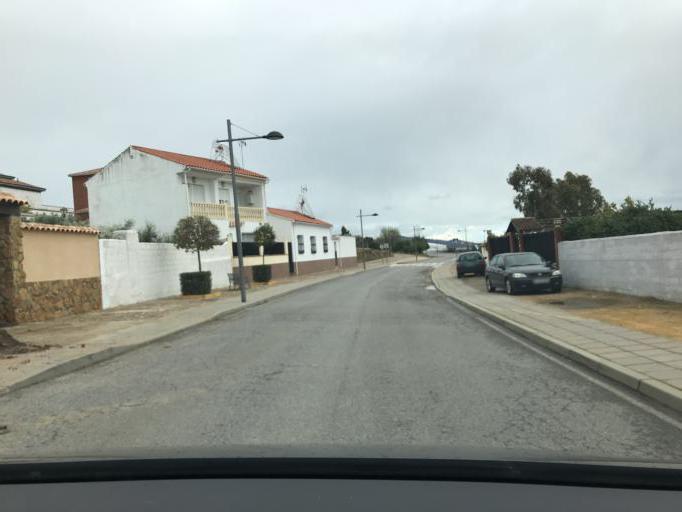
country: ES
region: Andalusia
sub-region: Province of Cordoba
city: Fuente Obejuna
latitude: 38.2637
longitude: -5.4171
